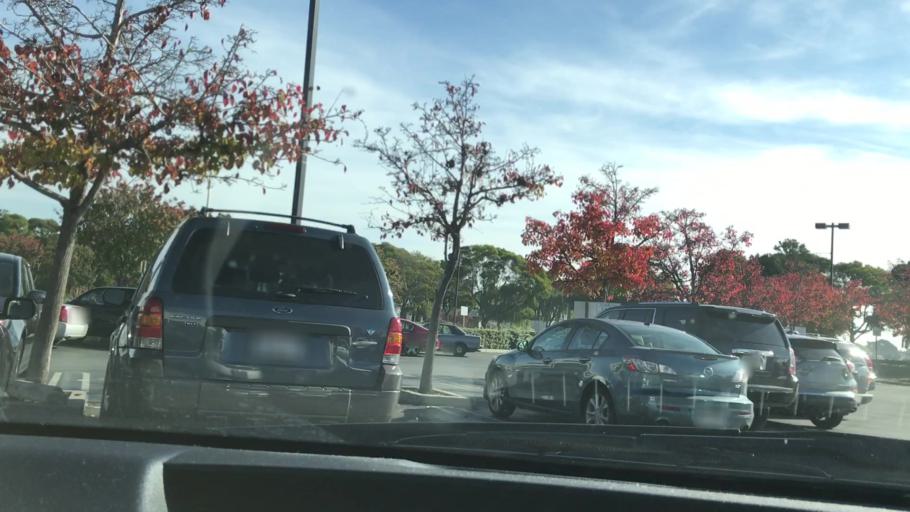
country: US
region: California
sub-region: San Mateo County
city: Foster City
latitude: 37.5574
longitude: -122.2744
